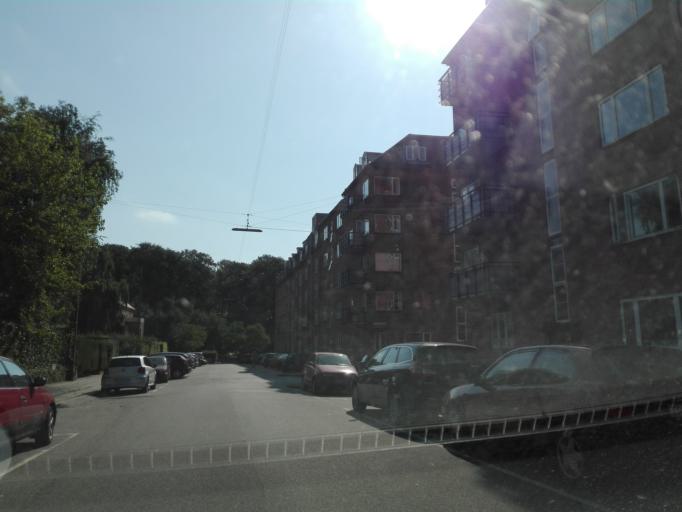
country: DK
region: Central Jutland
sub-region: Arhus Kommune
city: Arhus
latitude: 56.1715
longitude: 10.2181
